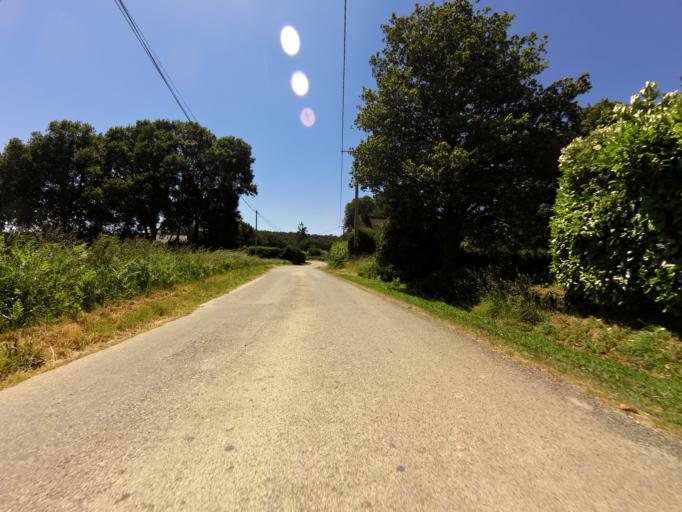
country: FR
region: Brittany
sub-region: Departement du Morbihan
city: Molac
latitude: 47.7145
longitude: -2.4143
